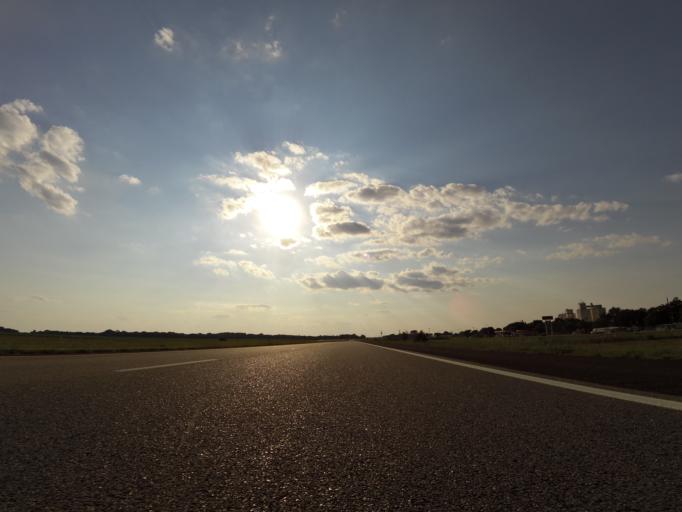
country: US
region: Kansas
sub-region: Reno County
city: Haven
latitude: 37.8956
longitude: -97.7786
